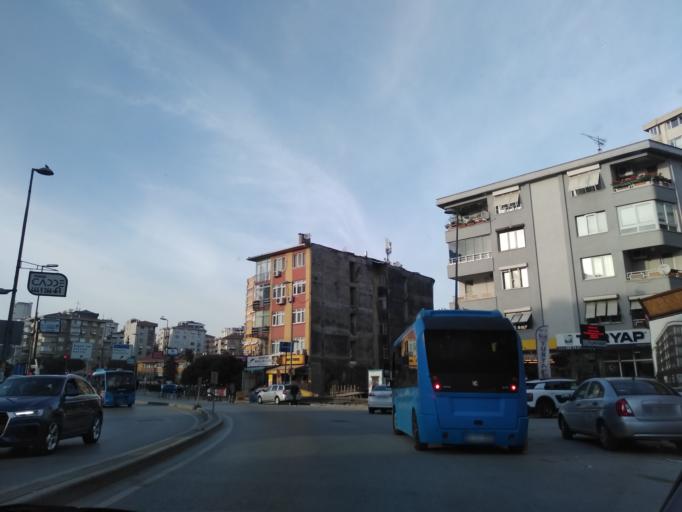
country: TR
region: Istanbul
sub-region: Atasehir
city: Atasehir
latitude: 40.9550
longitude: 29.1008
